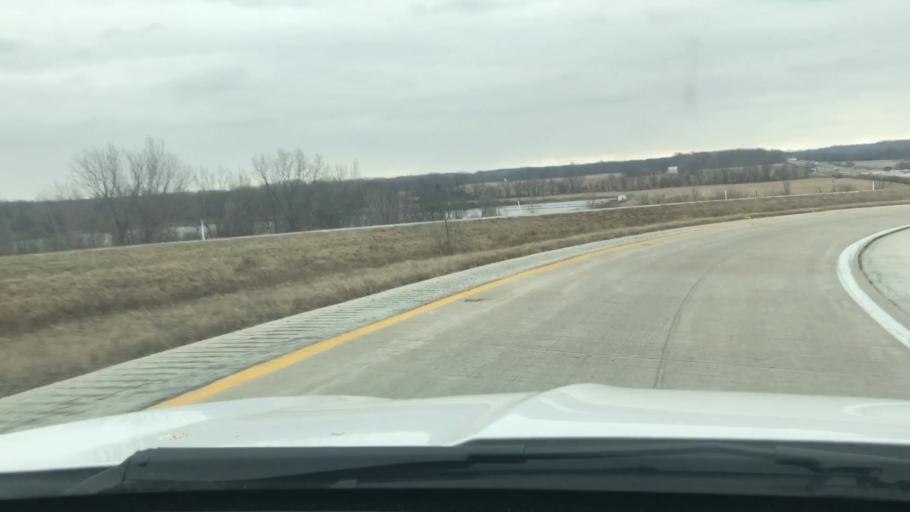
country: US
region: Indiana
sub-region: Miami County
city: Peru
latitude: 40.7712
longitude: -86.1259
